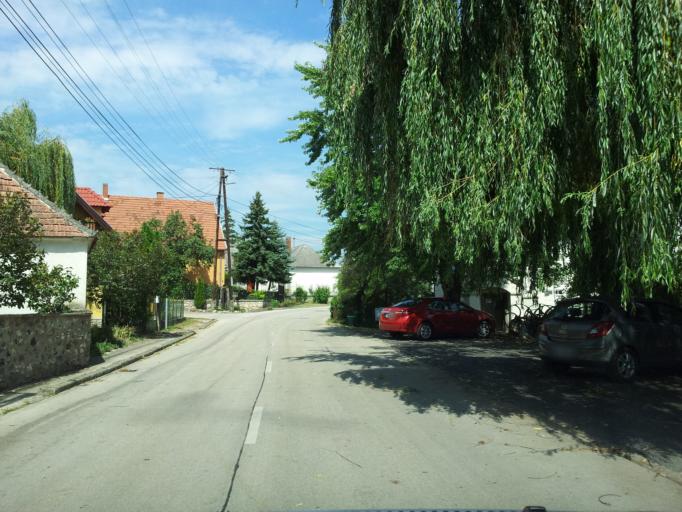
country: HU
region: Veszprem
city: Tapolca
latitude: 46.8871
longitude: 17.4969
